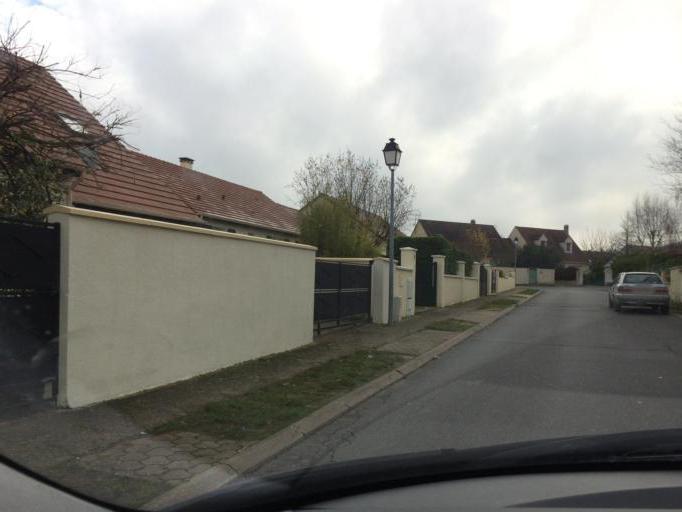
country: FR
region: Ile-de-France
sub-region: Departement de l'Essonne
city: Etrechy
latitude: 48.4858
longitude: 2.1866
